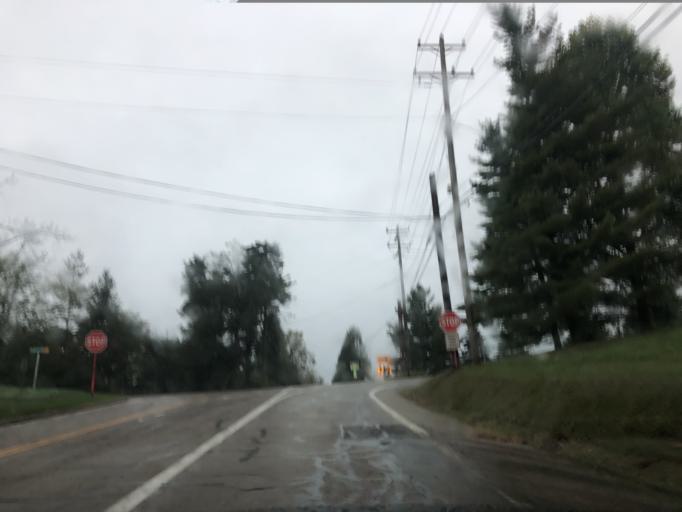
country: US
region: Ohio
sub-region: Hamilton County
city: The Village of Indian Hill
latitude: 39.2329
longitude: -84.3216
